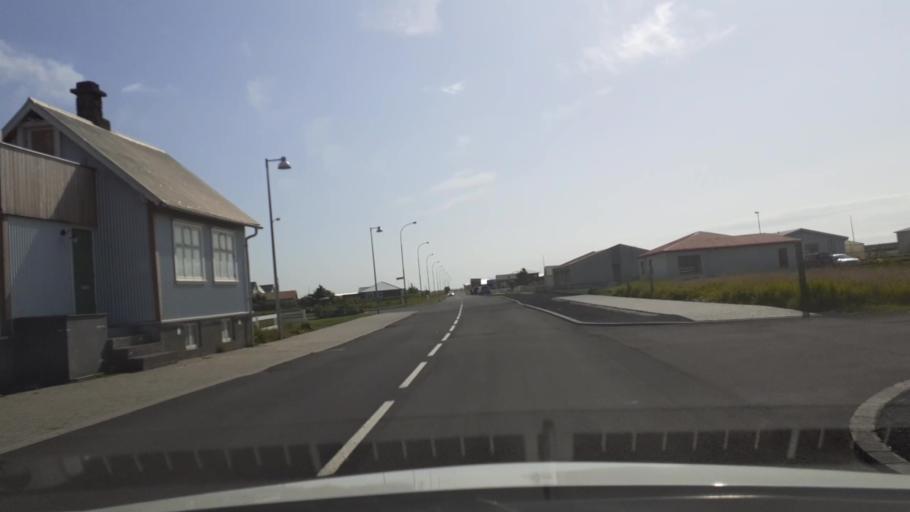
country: IS
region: South
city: Hveragerdi
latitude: 63.8611
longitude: -21.1437
